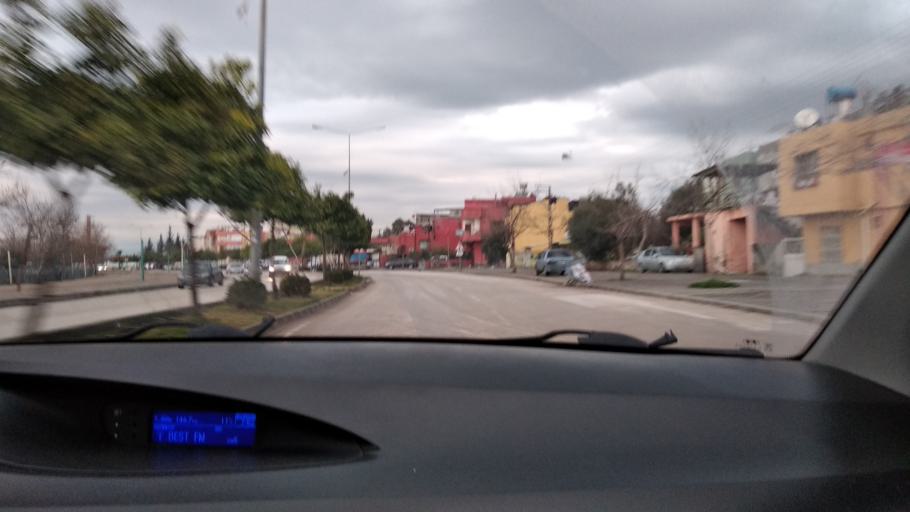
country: TR
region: Adana
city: Yuregir
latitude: 37.0141
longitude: 35.3864
